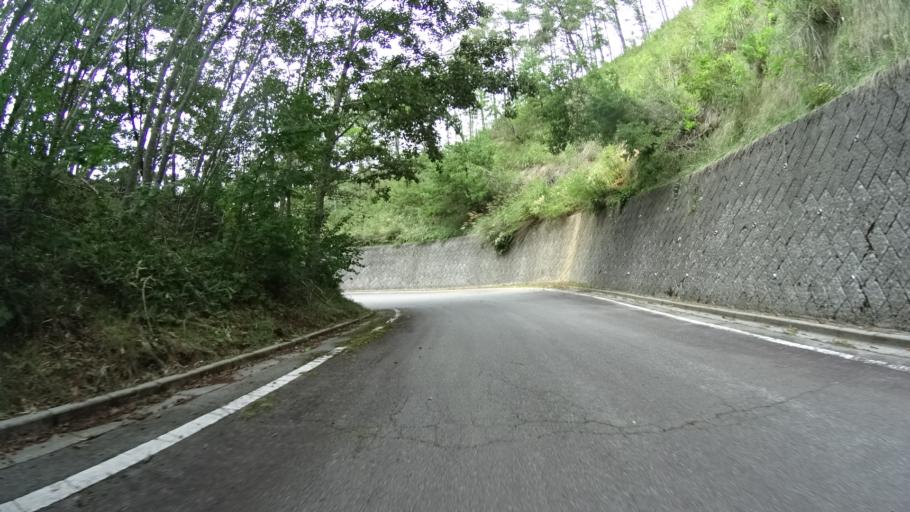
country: JP
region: Yamanashi
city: Kofu-shi
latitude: 35.8310
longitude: 138.5602
